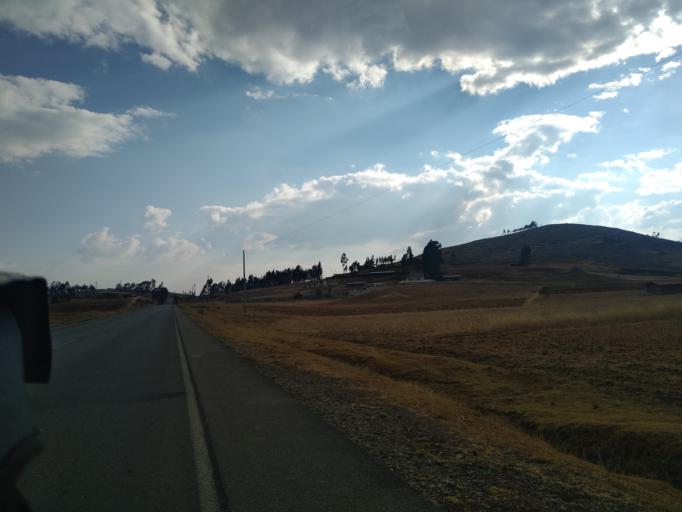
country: PE
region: Cajamarca
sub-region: Provincia de Cajamarca
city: Encanada
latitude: -7.1411
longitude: -78.3899
